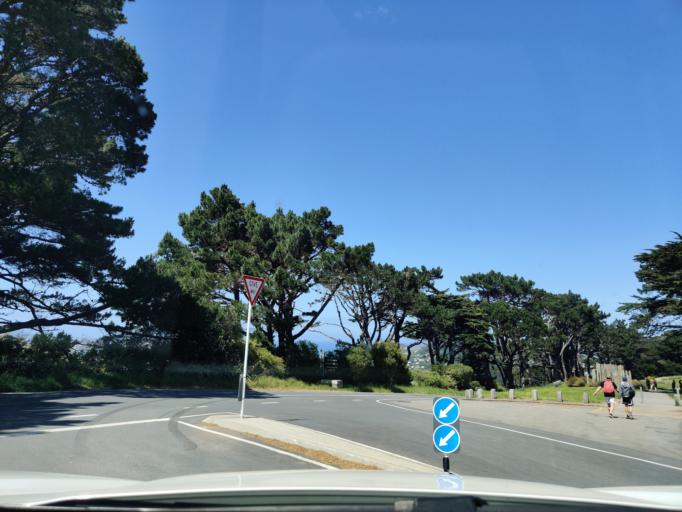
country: NZ
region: Wellington
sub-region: Wellington City
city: Wellington
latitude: -41.2977
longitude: 174.7932
